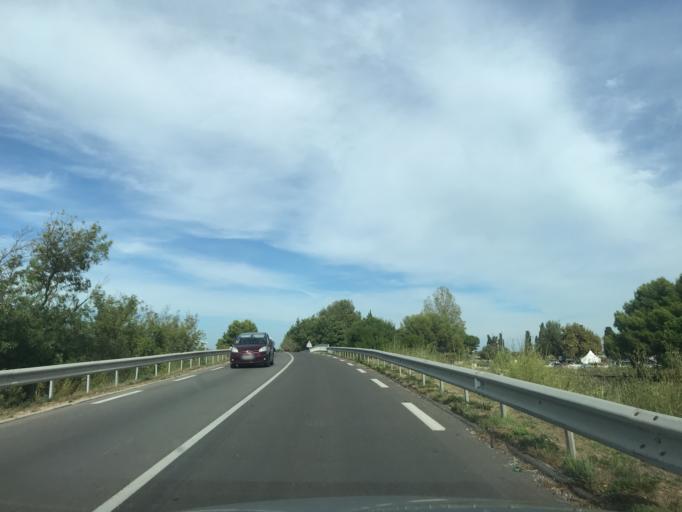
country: FR
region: Languedoc-Roussillon
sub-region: Departement du Gard
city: Aigues-Mortes
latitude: 43.5567
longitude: 4.1806
